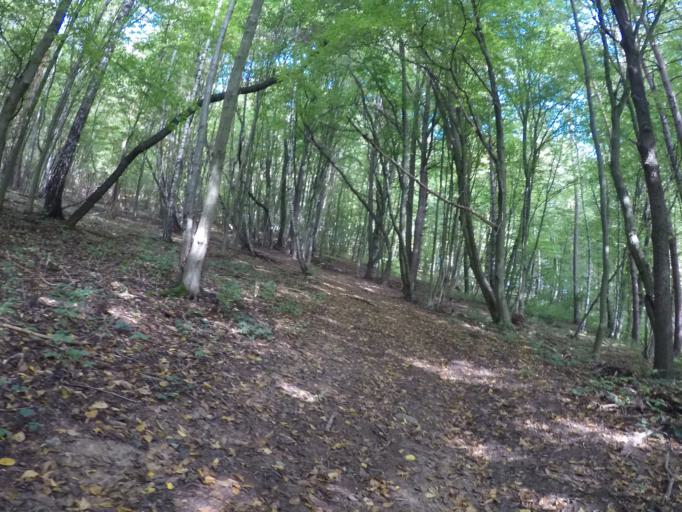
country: SK
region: Presovsky
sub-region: Okres Presov
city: Presov
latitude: 48.9388
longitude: 21.1471
